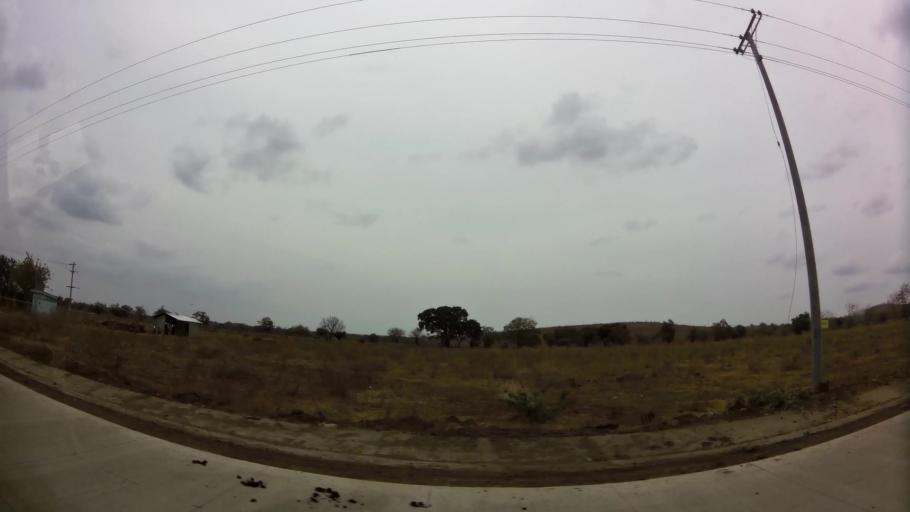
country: NI
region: Managua
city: Managua
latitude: 12.1039
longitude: -86.1753
